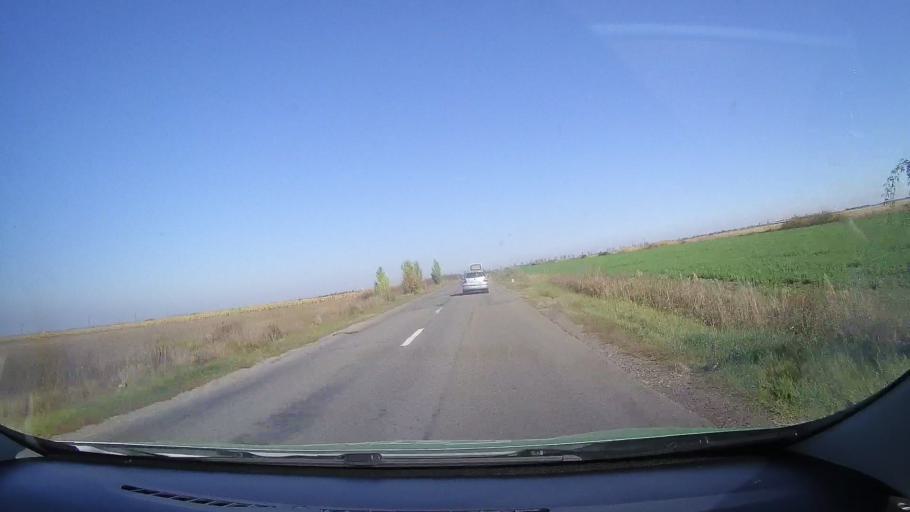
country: RO
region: Satu Mare
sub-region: Comuna Cauas
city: Cauas
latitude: 47.5828
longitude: 22.5476
